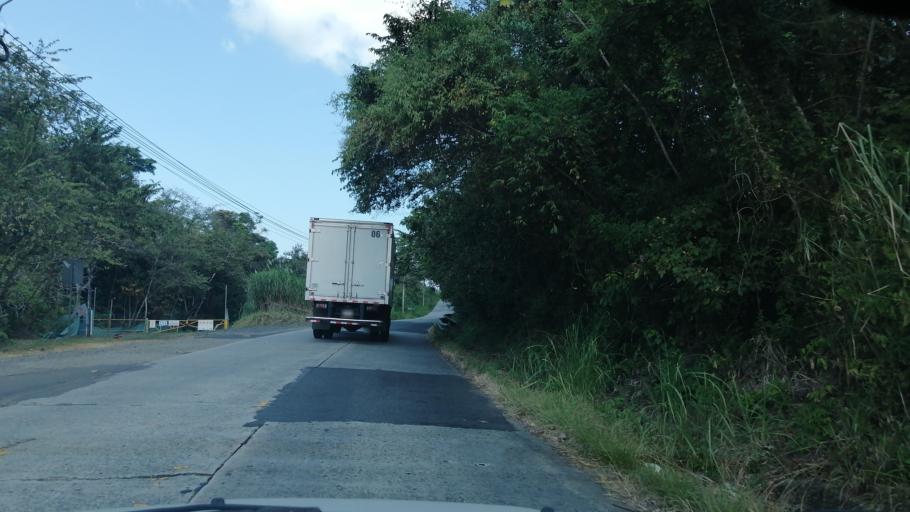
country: PA
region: Panama
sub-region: Distrito de Panama
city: Ancon
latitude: 8.9356
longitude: -79.5738
